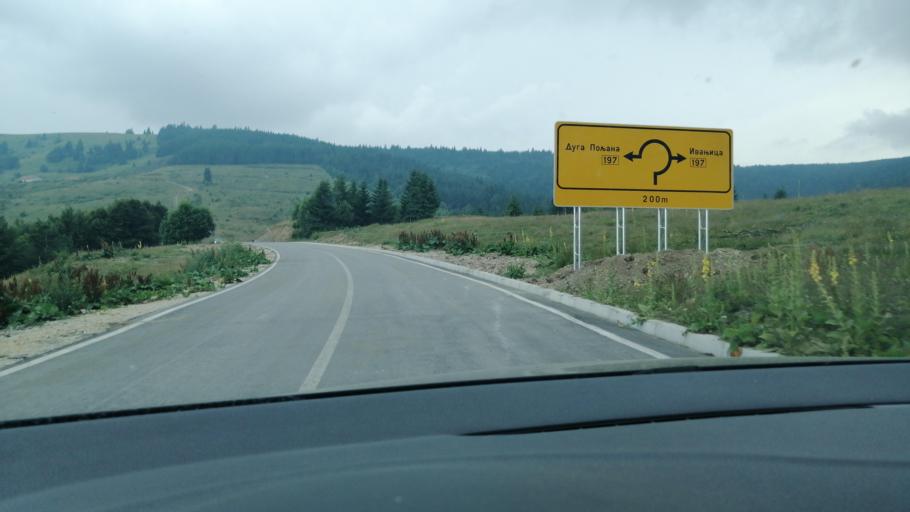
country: RS
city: Sokolovica
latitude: 43.3338
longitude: 20.2486
